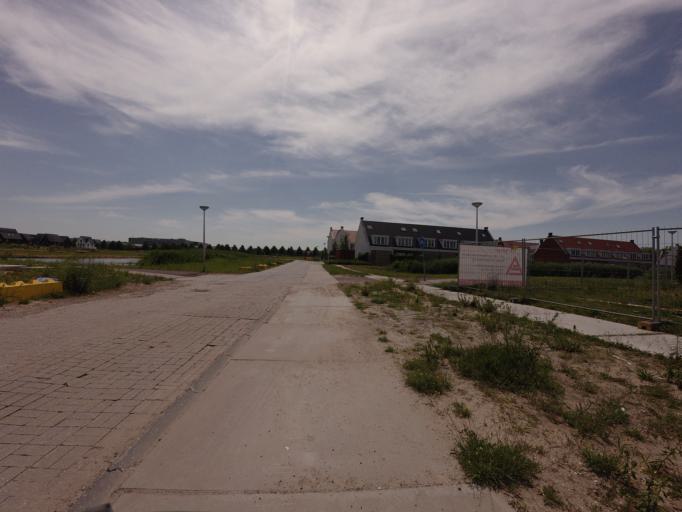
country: NL
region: South Holland
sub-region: Bodegraven-Reeuwijk
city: Bodegraven
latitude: 52.0751
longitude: 4.7624
